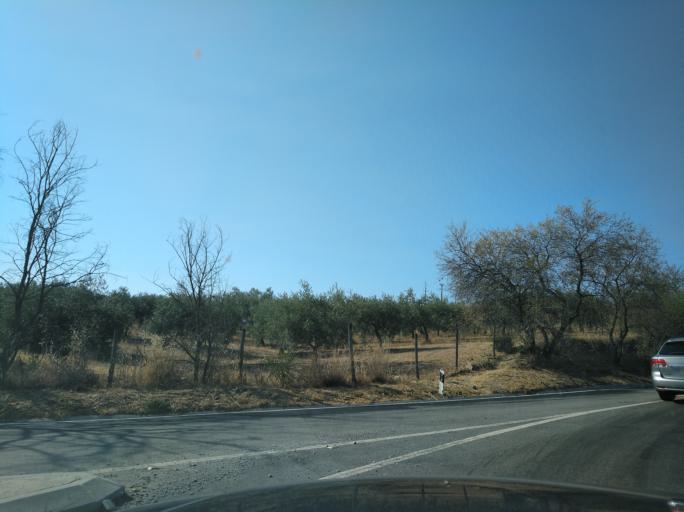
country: ES
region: Andalusia
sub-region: Provincia de Huelva
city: Rosal de la Frontera
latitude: 37.9496
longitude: -7.3029
